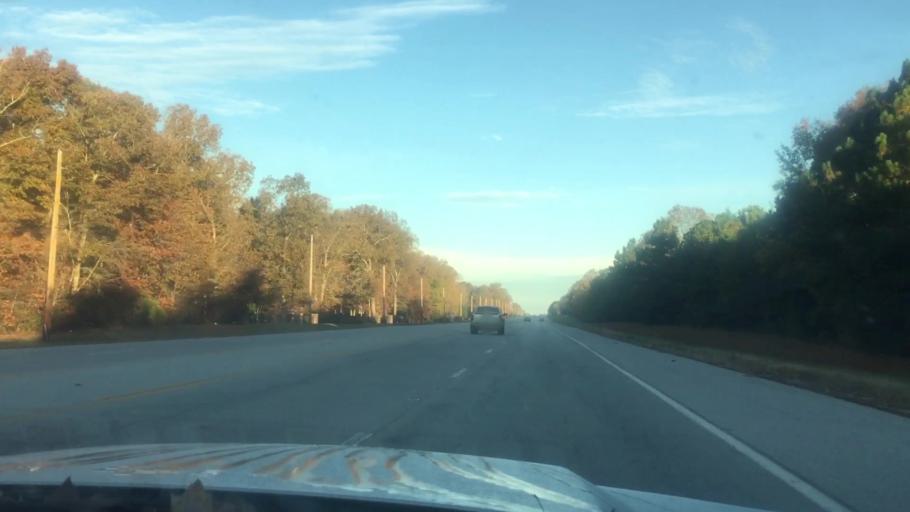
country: US
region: Tennessee
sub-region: Franklin County
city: Estill Springs
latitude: 35.3139
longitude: -86.1662
